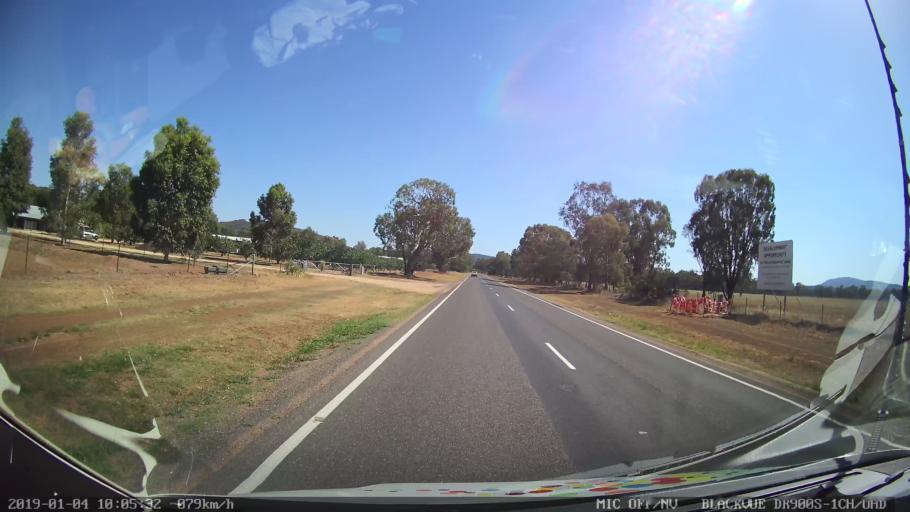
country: AU
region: New South Wales
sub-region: Cabonne
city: Canowindra
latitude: -33.4406
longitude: 148.3655
